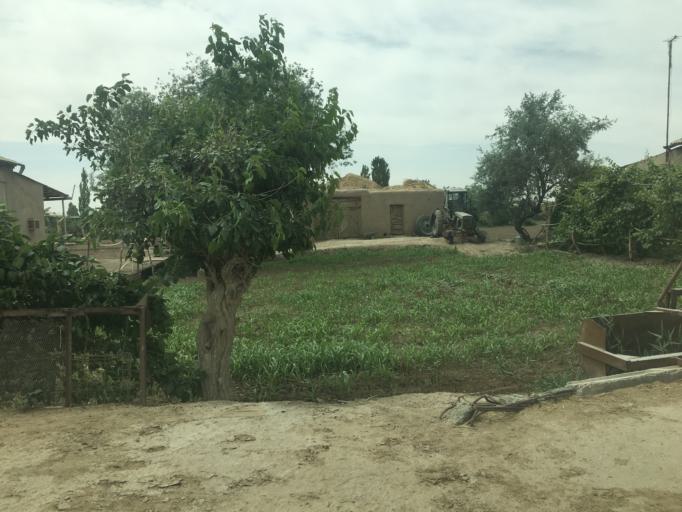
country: TM
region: Dasoguz
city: Tagta
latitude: 41.6137
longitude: 59.8275
